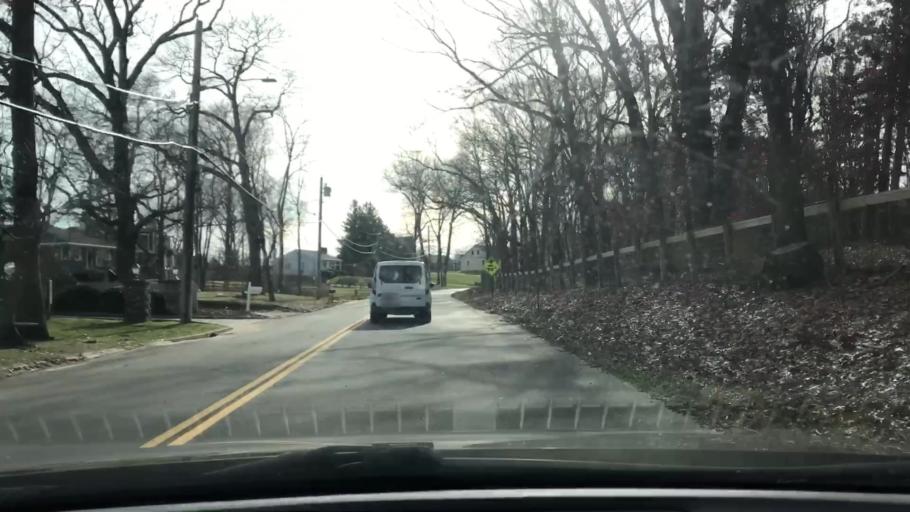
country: US
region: New York
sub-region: Suffolk County
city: Aquebogue
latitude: 40.9528
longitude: -72.6208
